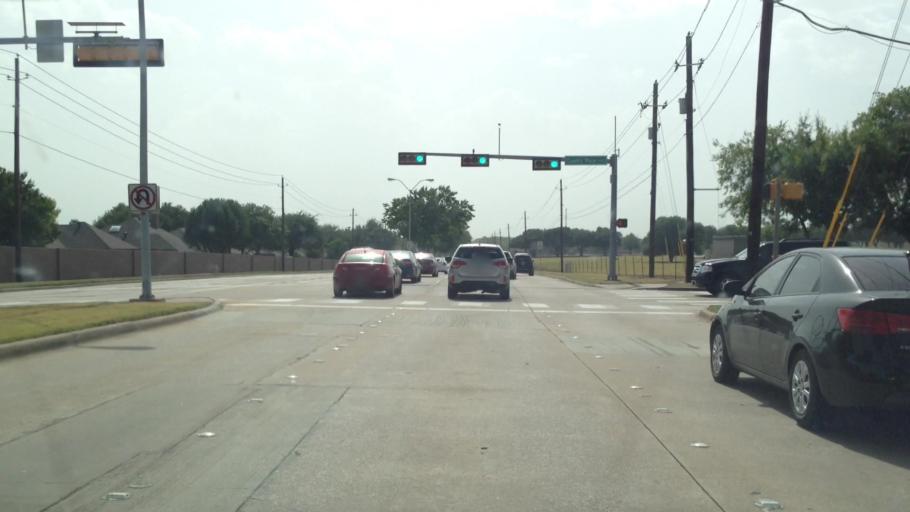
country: US
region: Texas
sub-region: Collin County
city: Plano
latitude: 33.0265
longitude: -96.7264
